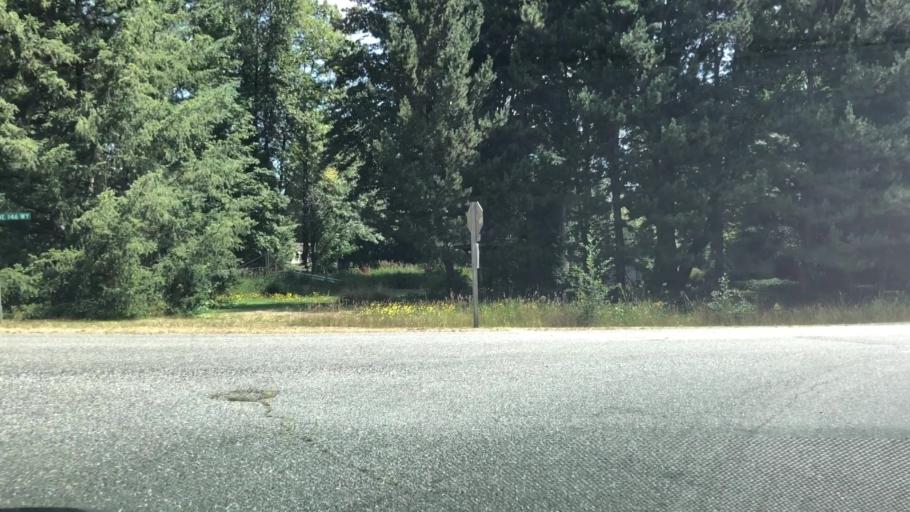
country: US
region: Washington
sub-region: King County
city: Cottage Lake
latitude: 47.7359
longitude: -122.0916
